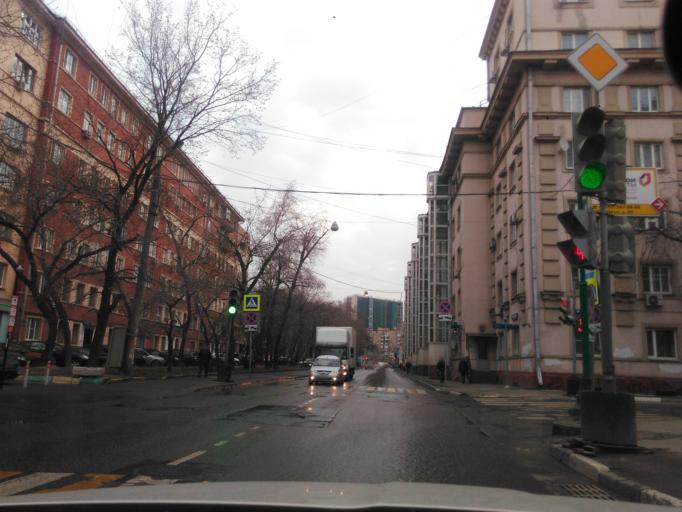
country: RU
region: Moskovskaya
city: Dorogomilovo
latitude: 55.7894
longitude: 37.5752
